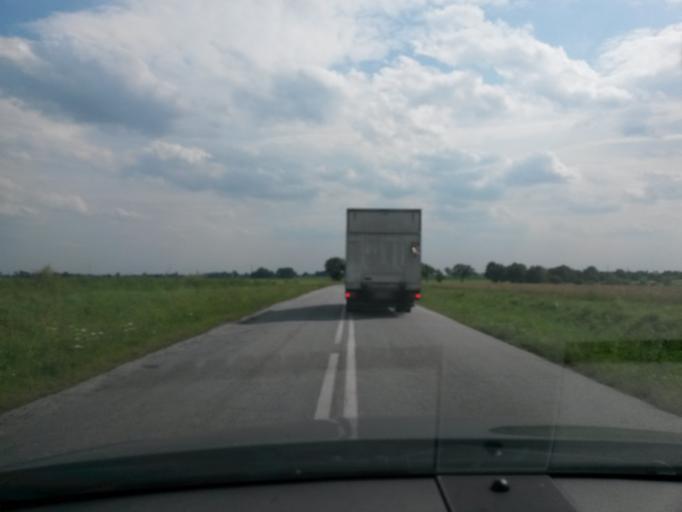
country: PL
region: Greater Poland Voivodeship
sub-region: Powiat poznanski
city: Kornik
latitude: 52.2968
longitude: 17.1228
